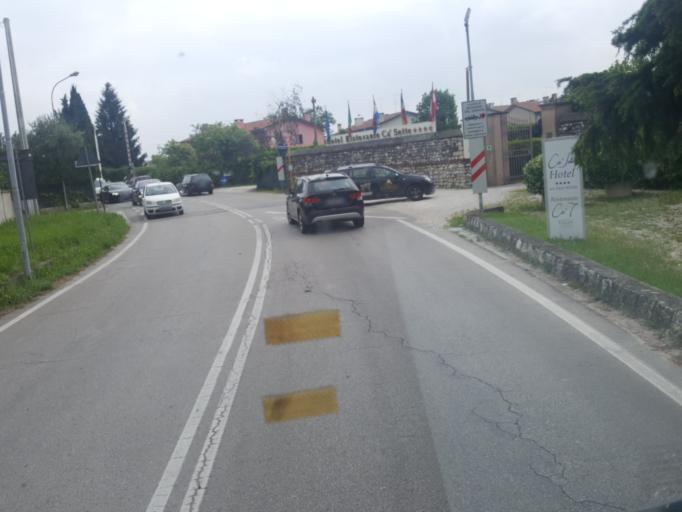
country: IT
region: Veneto
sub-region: Provincia di Vicenza
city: Bassano del Grappa
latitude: 45.7794
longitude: 11.7417
